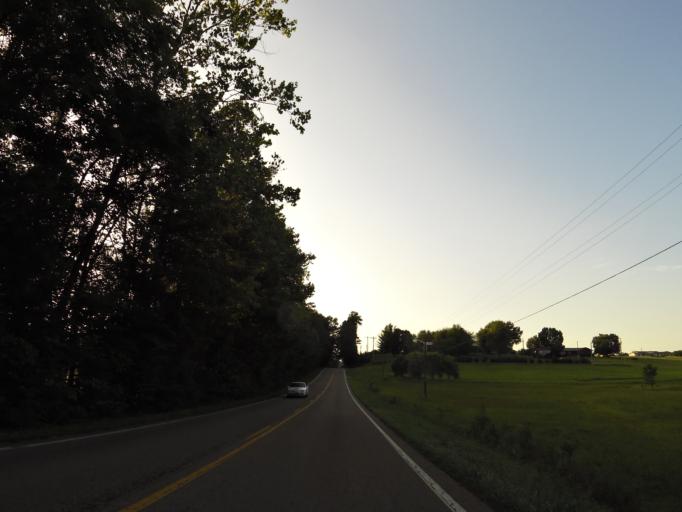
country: US
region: Tennessee
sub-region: Jefferson County
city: White Pine
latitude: 36.0011
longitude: -83.2948
